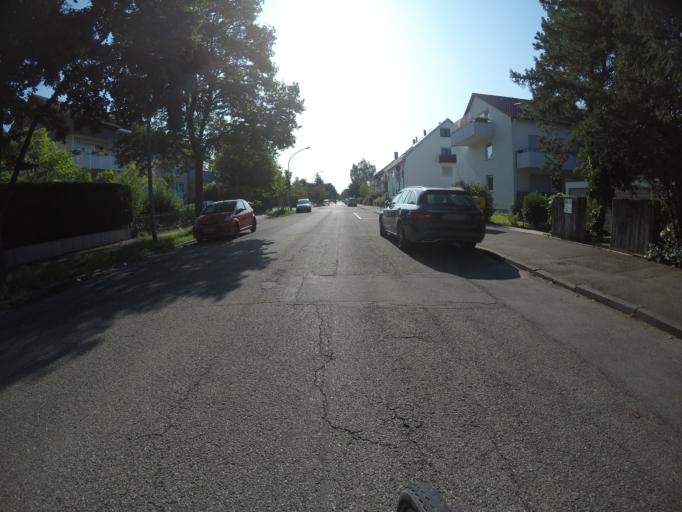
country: DE
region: Baden-Wuerttemberg
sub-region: Regierungsbezirk Stuttgart
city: Leinfelden-Echterdingen
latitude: 48.7152
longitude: 9.2017
